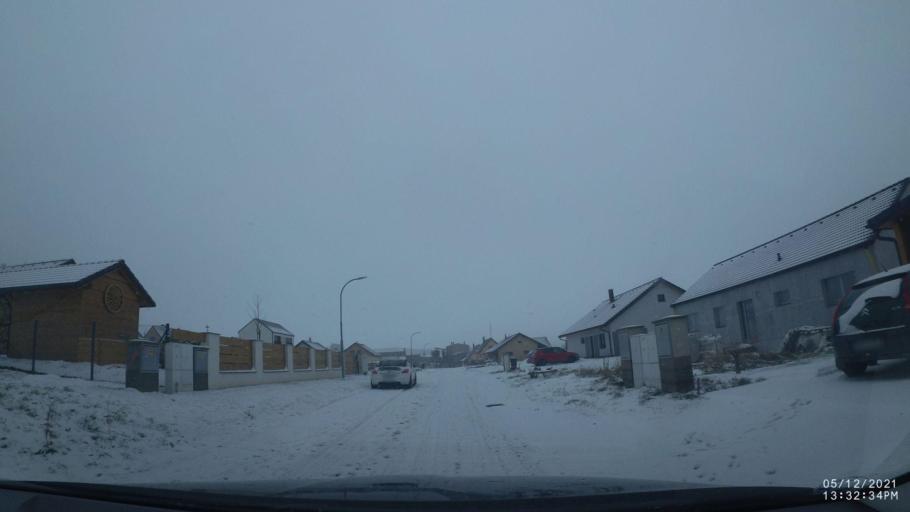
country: CZ
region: Kralovehradecky
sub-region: Okres Nachod
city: Police nad Metuji
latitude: 50.5057
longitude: 16.2290
